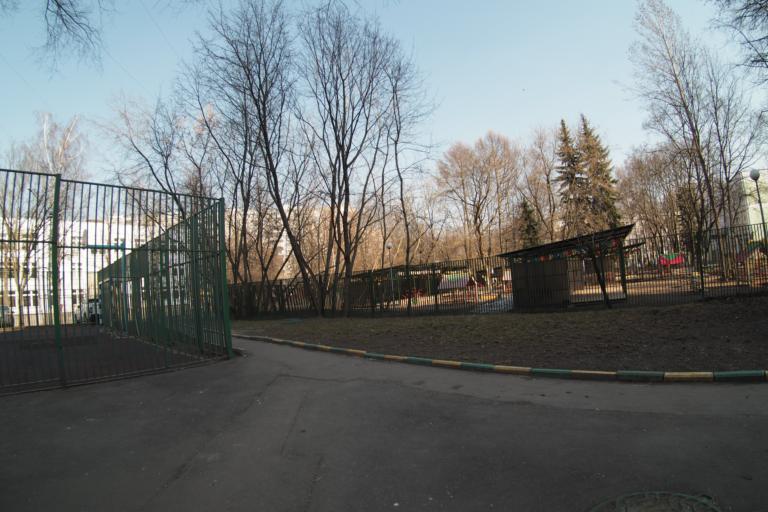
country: RU
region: Moscow
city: Matveyevskoye
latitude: 55.7108
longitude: 37.4832
